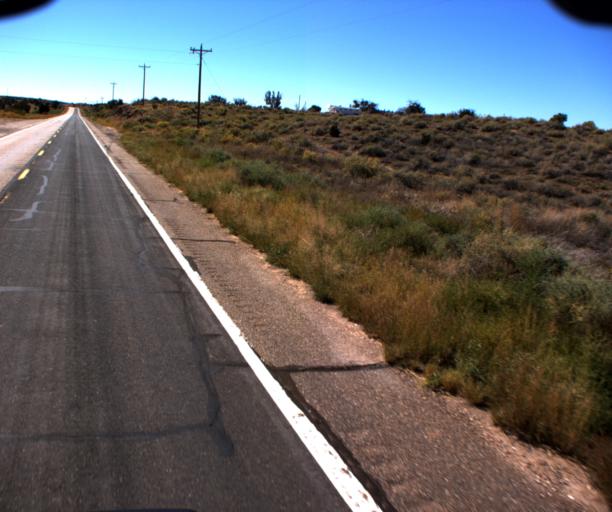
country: US
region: Arizona
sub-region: Apache County
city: Saint Johns
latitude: 34.4113
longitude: -109.4107
